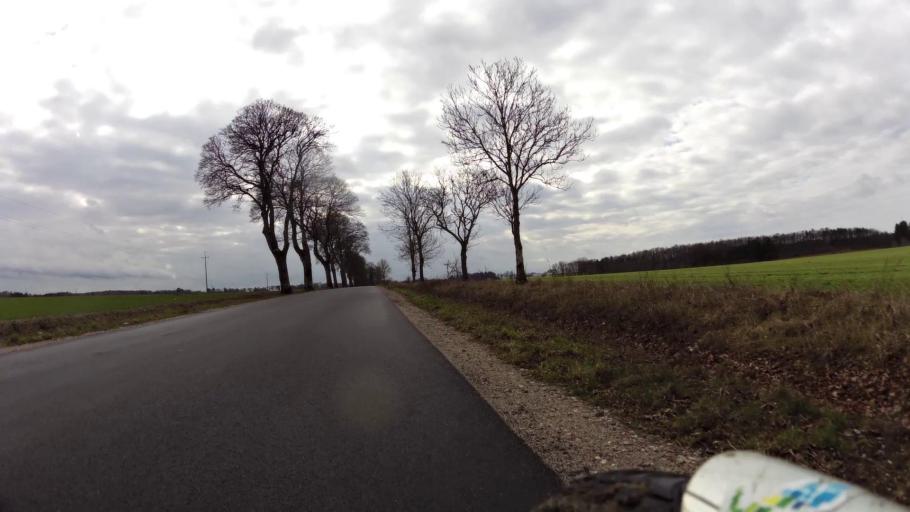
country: PL
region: Pomeranian Voivodeship
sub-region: Powiat bytowski
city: Kolczyglowy
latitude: 54.2343
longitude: 17.2424
